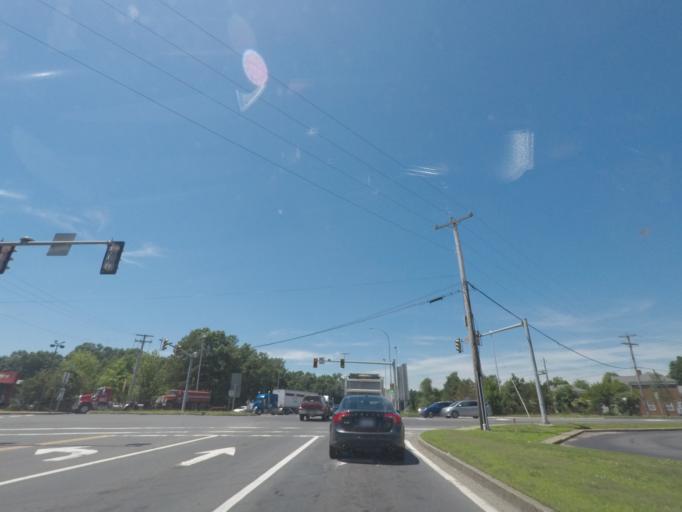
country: US
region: Massachusetts
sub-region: Hampden County
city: Westfield
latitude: 42.1417
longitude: -72.7327
